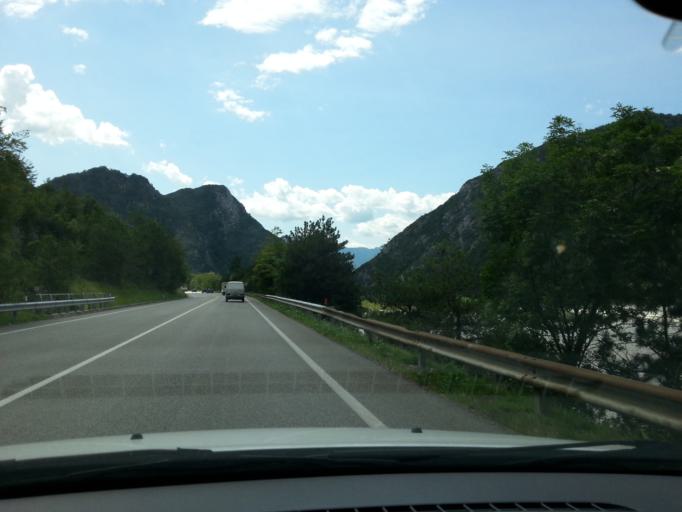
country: IT
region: Friuli Venezia Giulia
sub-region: Provincia di Udine
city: Moggio di Sotto
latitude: 46.3951
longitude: 13.1690
